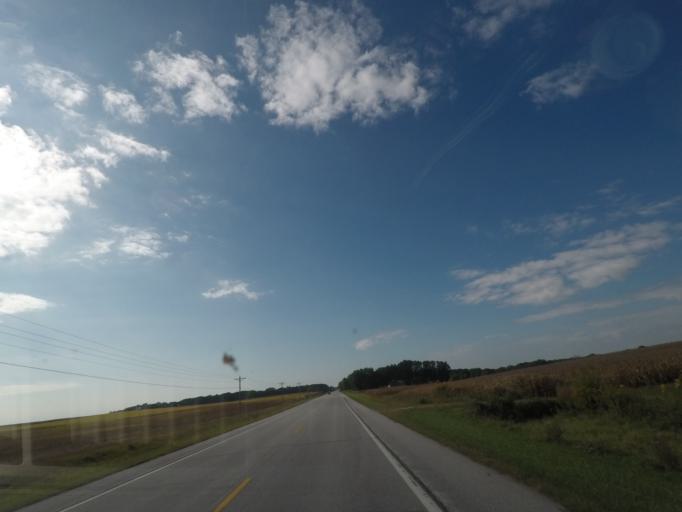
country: US
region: Iowa
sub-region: Story County
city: Nevada
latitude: 41.9992
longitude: -93.4446
